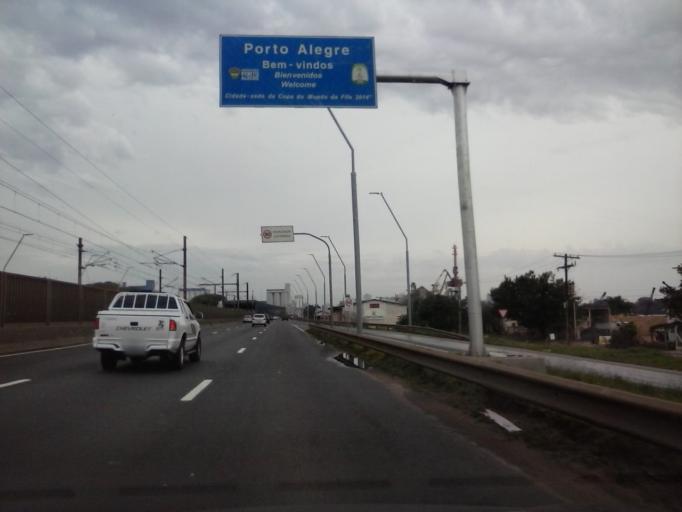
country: BR
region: Rio Grande do Sul
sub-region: Porto Alegre
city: Porto Alegre
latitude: -30.0032
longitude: -51.2084
